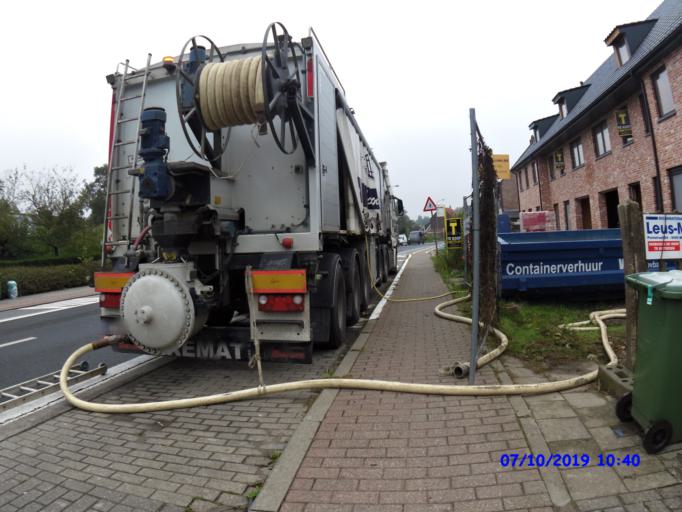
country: BE
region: Flanders
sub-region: Provincie Oost-Vlaanderen
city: Melle
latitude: 50.9811
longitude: 3.8006
